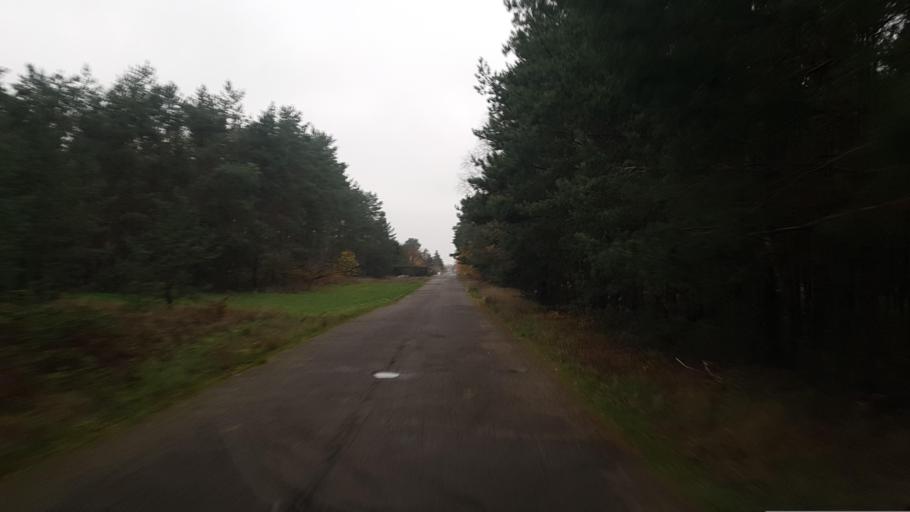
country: DE
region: Brandenburg
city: Ruhland
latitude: 51.4303
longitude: 13.8716
